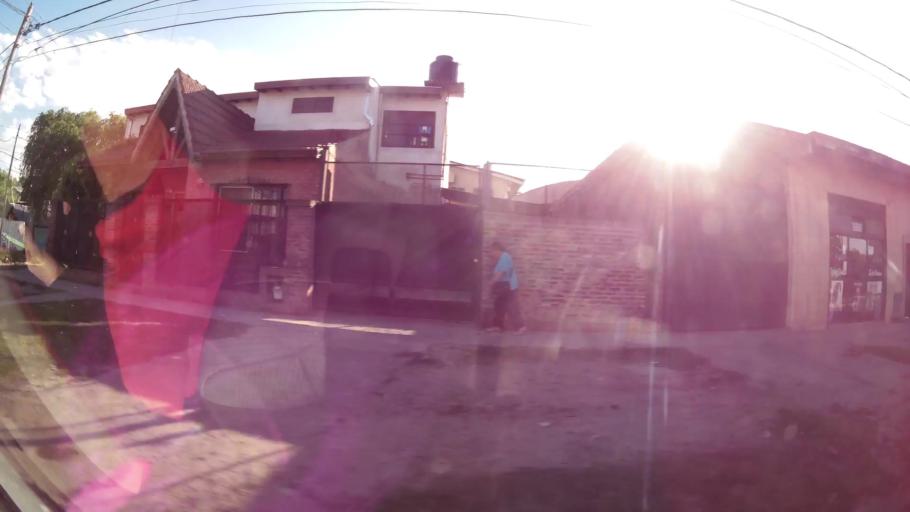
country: AR
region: Buenos Aires
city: Hurlingham
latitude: -34.5049
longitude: -58.7234
